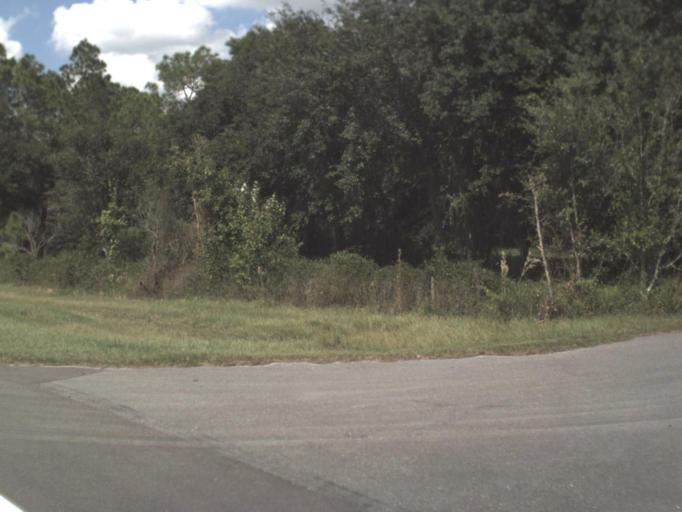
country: US
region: Florida
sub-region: Hardee County
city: Zolfo Springs
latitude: 27.4629
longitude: -81.6990
